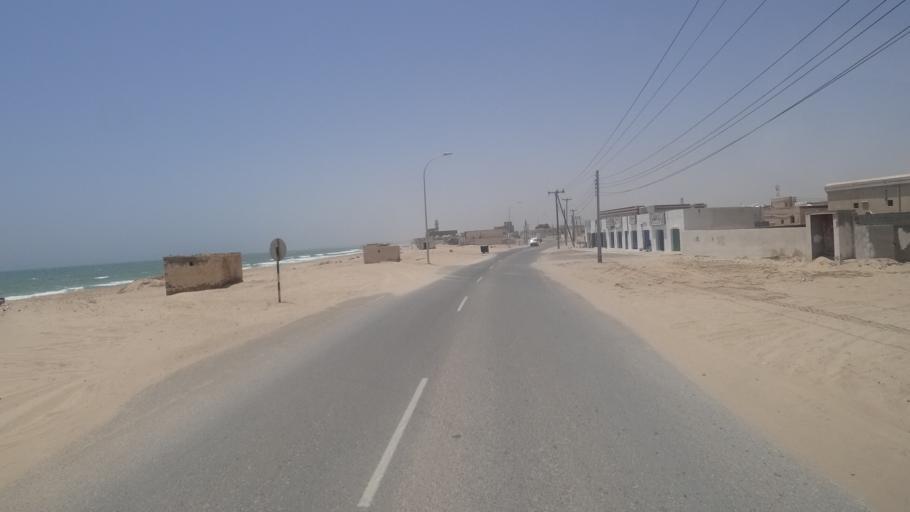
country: OM
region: Ash Sharqiyah
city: Sur
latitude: 22.0853
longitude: 59.6874
